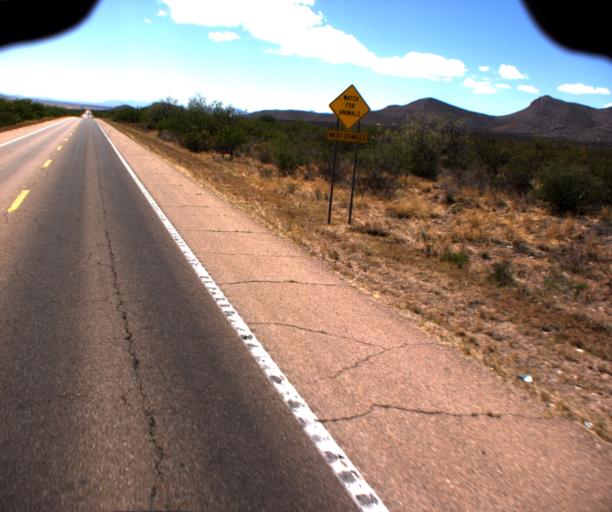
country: US
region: Arizona
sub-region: Cochise County
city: Naco
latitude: 31.3904
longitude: -109.9413
